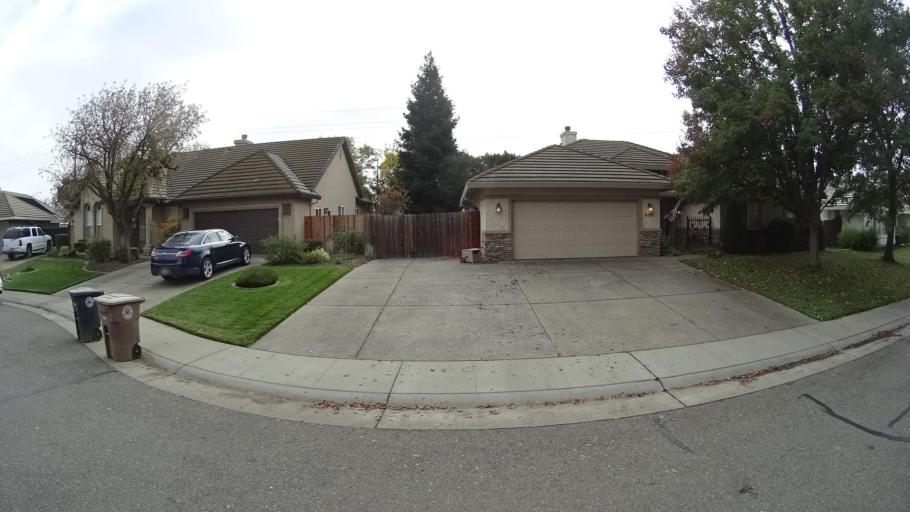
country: US
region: California
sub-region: Sacramento County
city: Elk Grove
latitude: 38.4242
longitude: -121.3675
